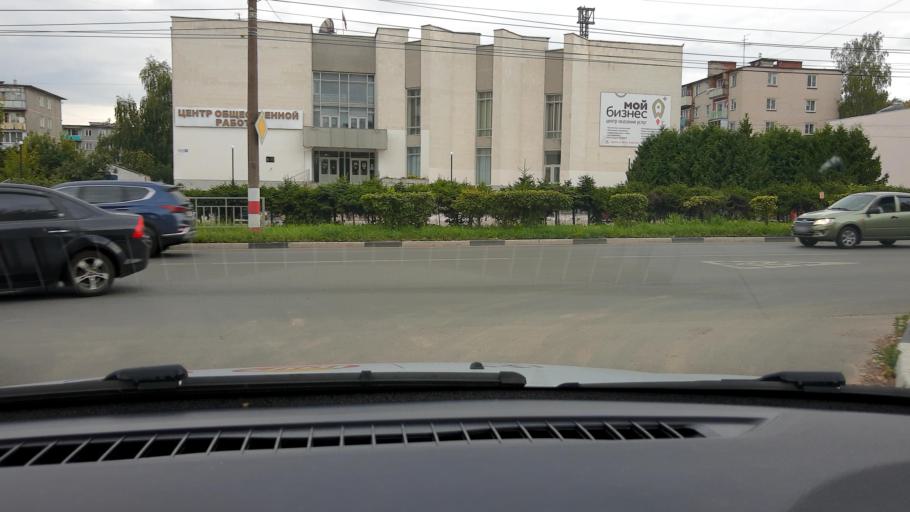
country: RU
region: Nizjnij Novgorod
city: Dzerzhinsk
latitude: 56.2325
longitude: 43.4574
